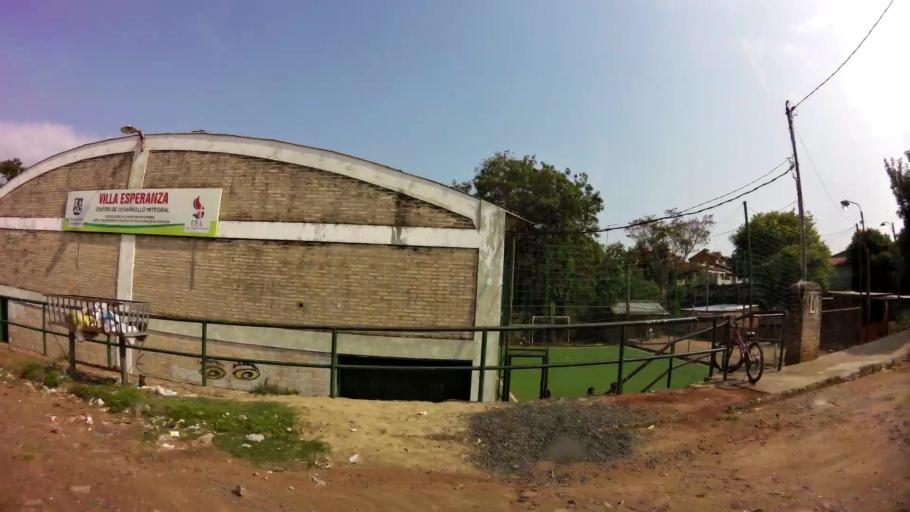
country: PY
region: Asuncion
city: Asuncion
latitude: -25.2982
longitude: -57.6592
